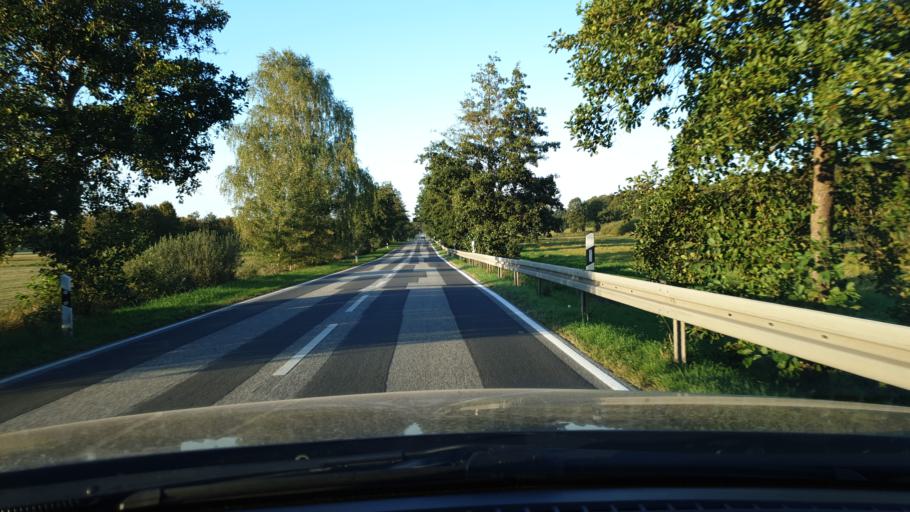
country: DE
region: Mecklenburg-Vorpommern
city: Wittenburg
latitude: 53.5512
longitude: 11.0909
